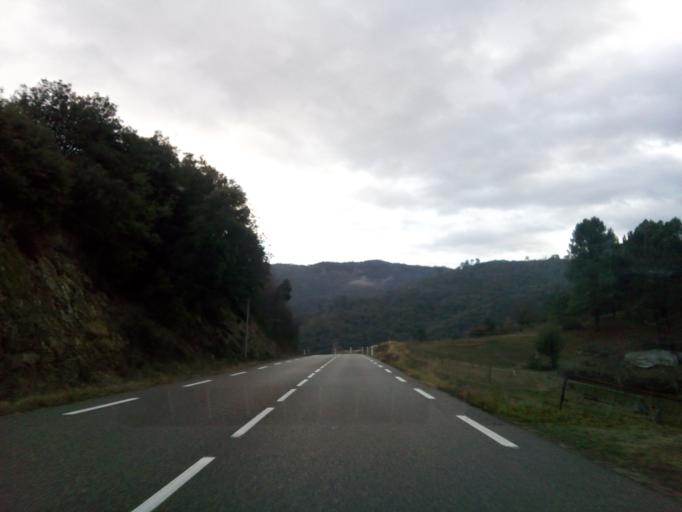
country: FR
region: Rhone-Alpes
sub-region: Departement de l'Ardeche
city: Saint-Laurent-du-Pape
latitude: 44.8175
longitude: 4.7092
